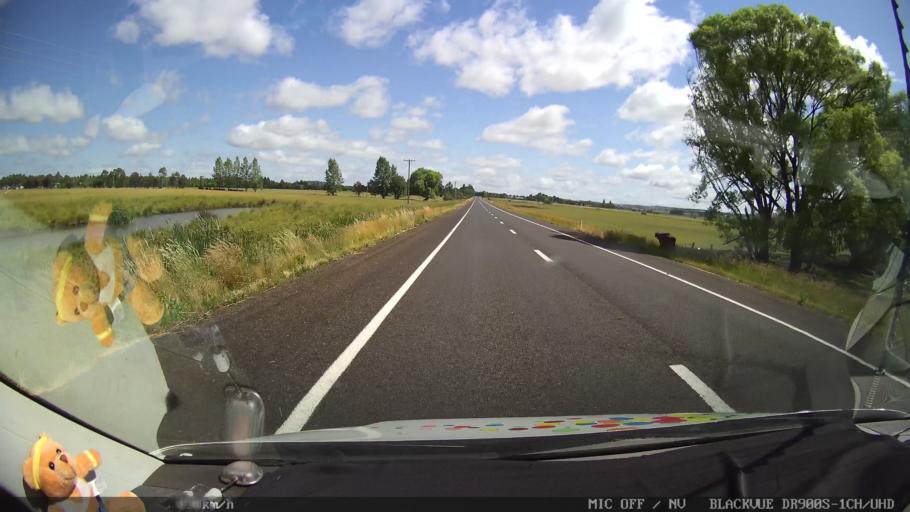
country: AU
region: New South Wales
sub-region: Glen Innes Severn
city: Glen Innes
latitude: -29.8306
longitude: 151.7378
